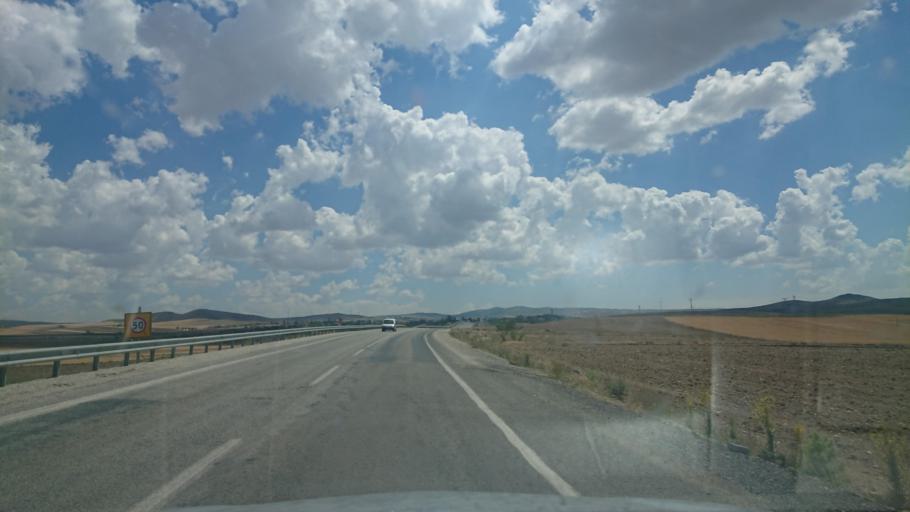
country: TR
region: Aksaray
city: Sariyahsi
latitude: 39.0026
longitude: 33.8557
